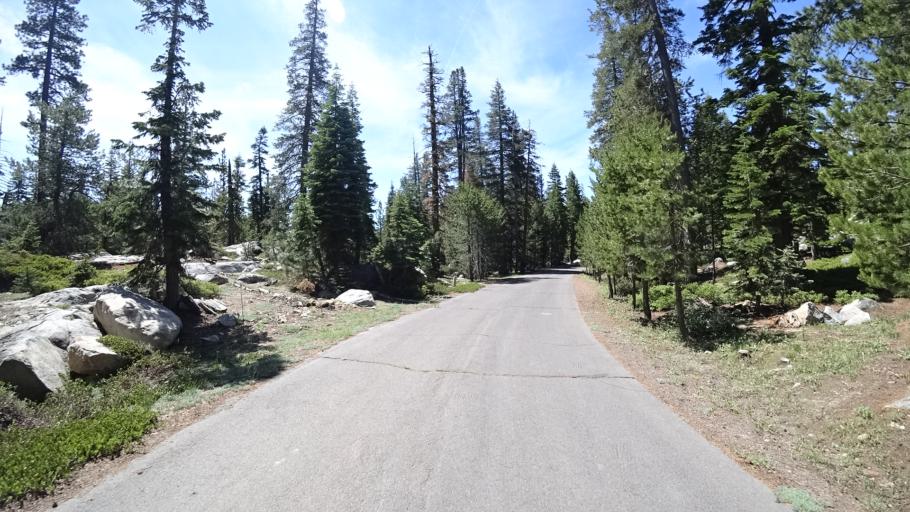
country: US
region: California
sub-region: Calaveras County
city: Arnold
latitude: 38.4400
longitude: -120.0805
